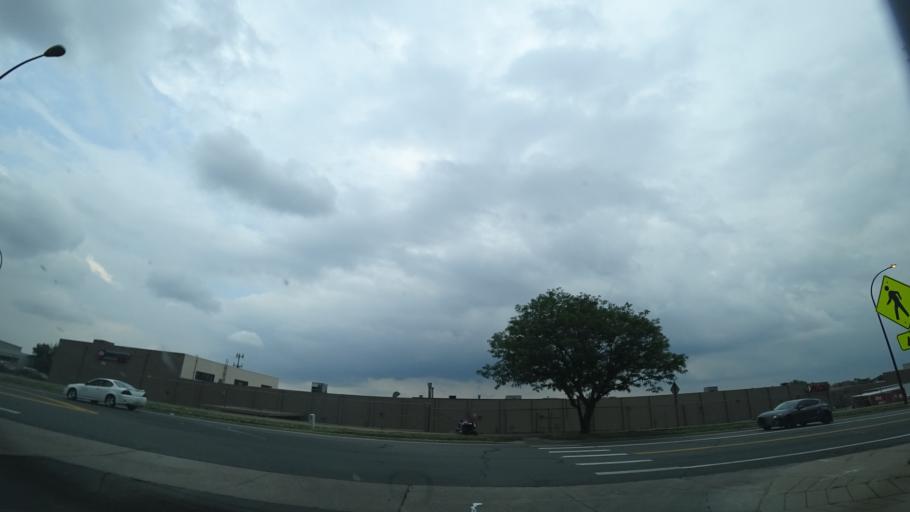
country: US
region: Colorado
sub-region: Jefferson County
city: West Pleasant View
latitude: 39.7100
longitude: -105.1383
